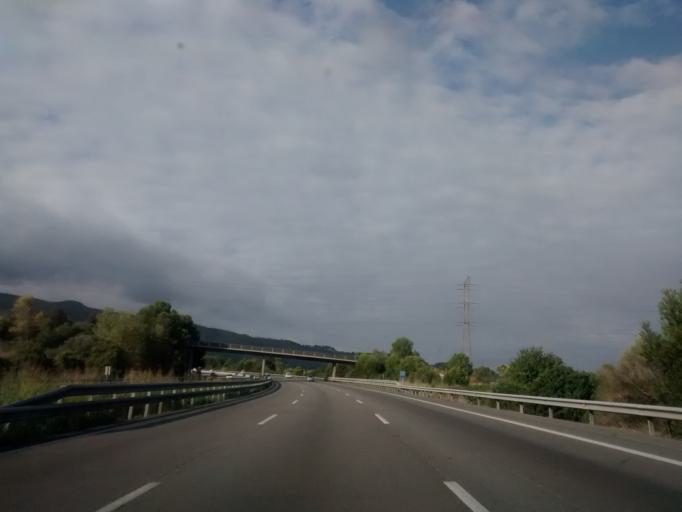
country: ES
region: Catalonia
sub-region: Provincia de Barcelona
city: Gelida
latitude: 41.4398
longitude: 1.8431
